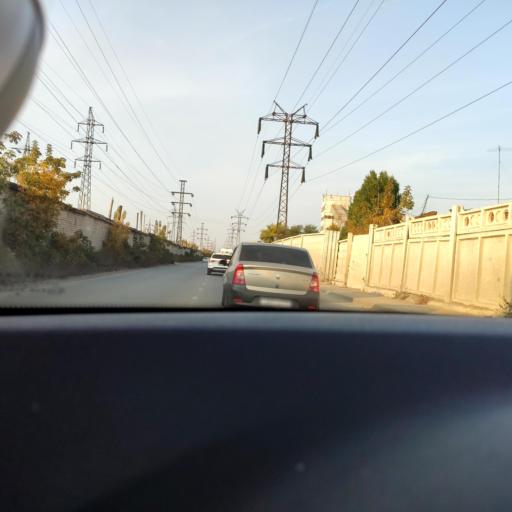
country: RU
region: Samara
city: Petra-Dubrava
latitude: 53.2482
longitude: 50.2933
